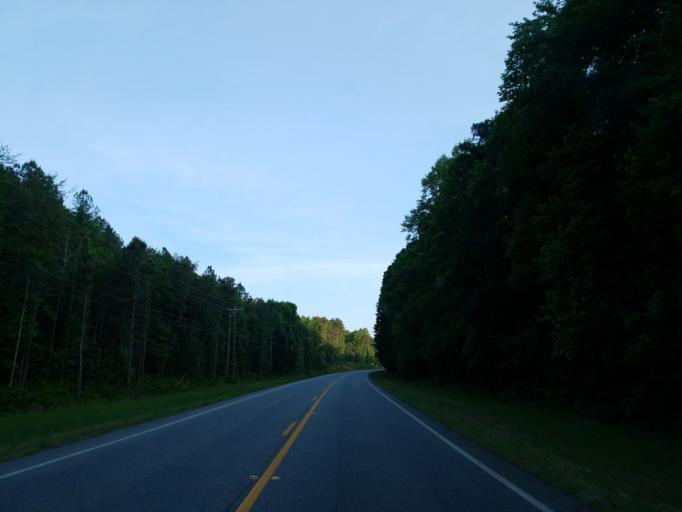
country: US
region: Georgia
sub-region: Whitfield County
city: Dalton
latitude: 34.6675
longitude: -85.0607
